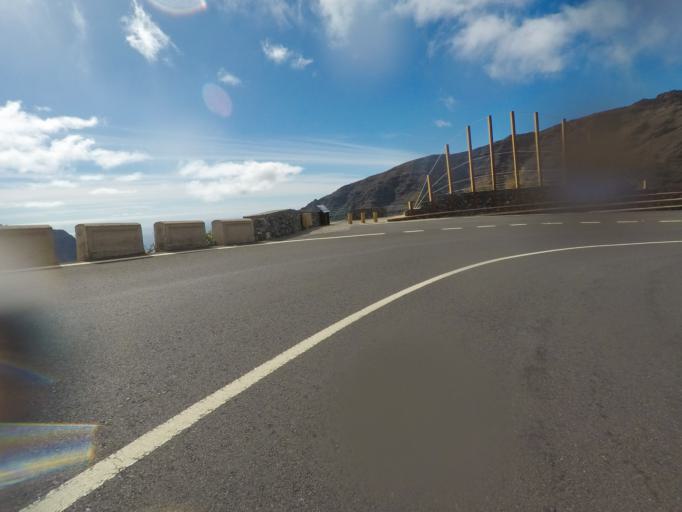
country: ES
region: Canary Islands
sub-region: Provincia de Santa Cruz de Tenerife
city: Vallehermosa
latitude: 28.1150
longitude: -17.3208
